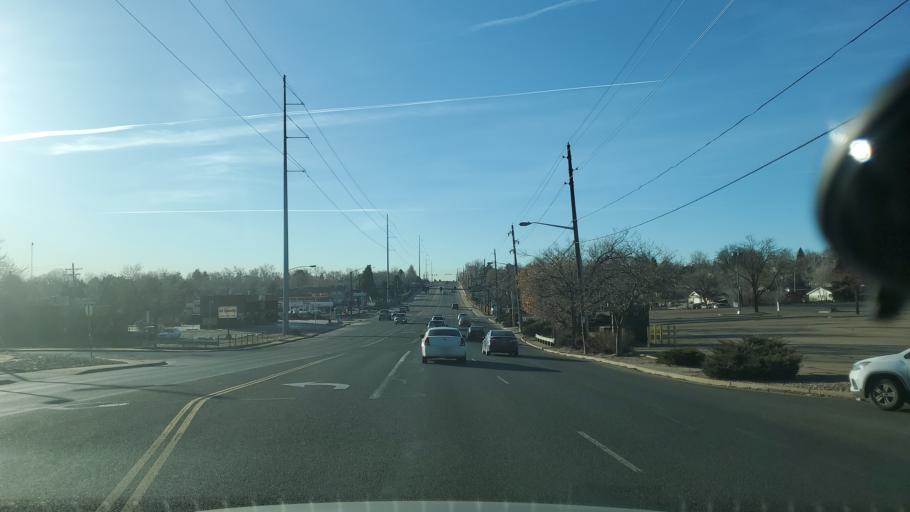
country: US
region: Colorado
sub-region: Adams County
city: Federal Heights
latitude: 39.8480
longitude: -104.9780
